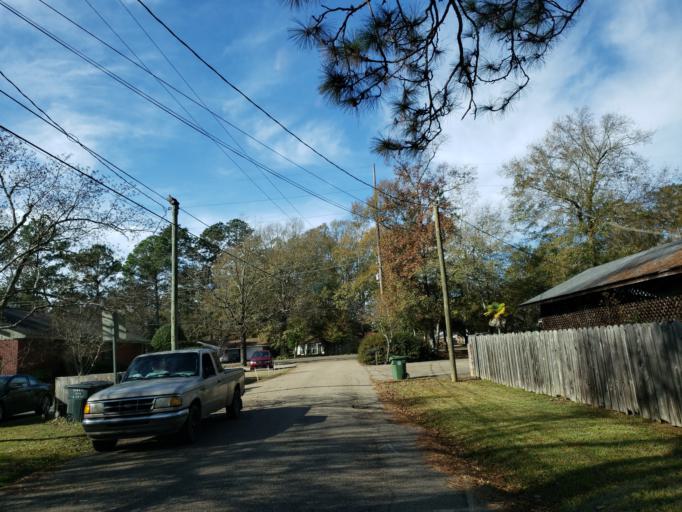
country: US
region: Mississippi
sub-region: Forrest County
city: Hattiesburg
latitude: 31.3068
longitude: -89.3304
